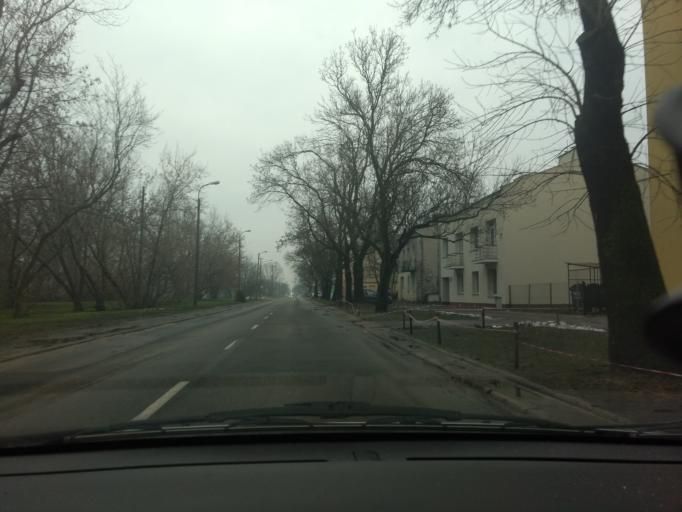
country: PL
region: Masovian Voivodeship
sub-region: Warszawa
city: Praga Polnoc
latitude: 52.2630
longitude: 21.0616
